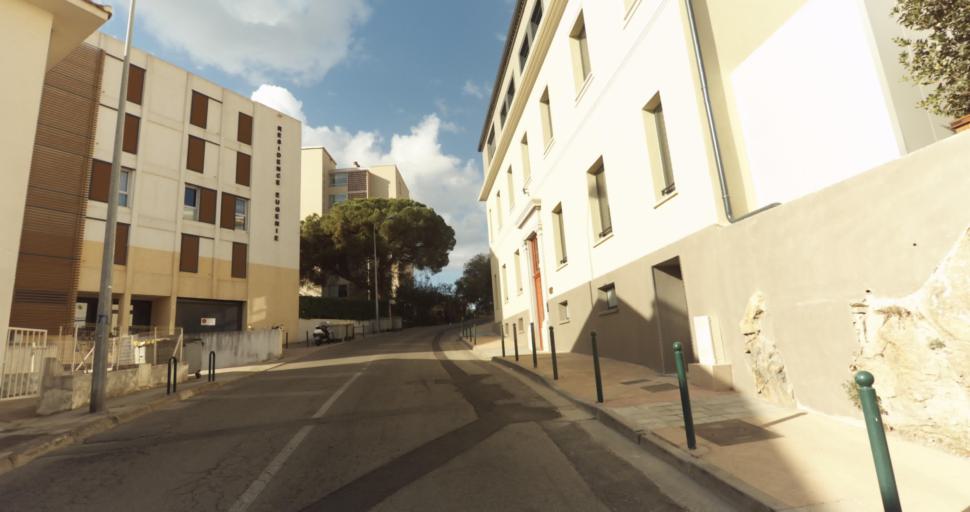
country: FR
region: Corsica
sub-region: Departement de la Corse-du-Sud
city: Ajaccio
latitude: 41.9198
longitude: 8.7339
